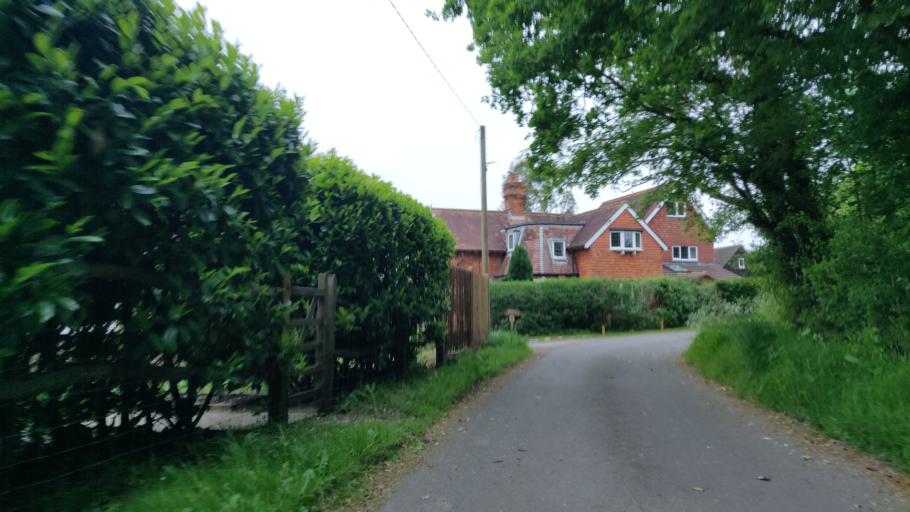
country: GB
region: England
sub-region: West Sussex
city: Southwater
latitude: 51.0153
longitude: -0.3324
